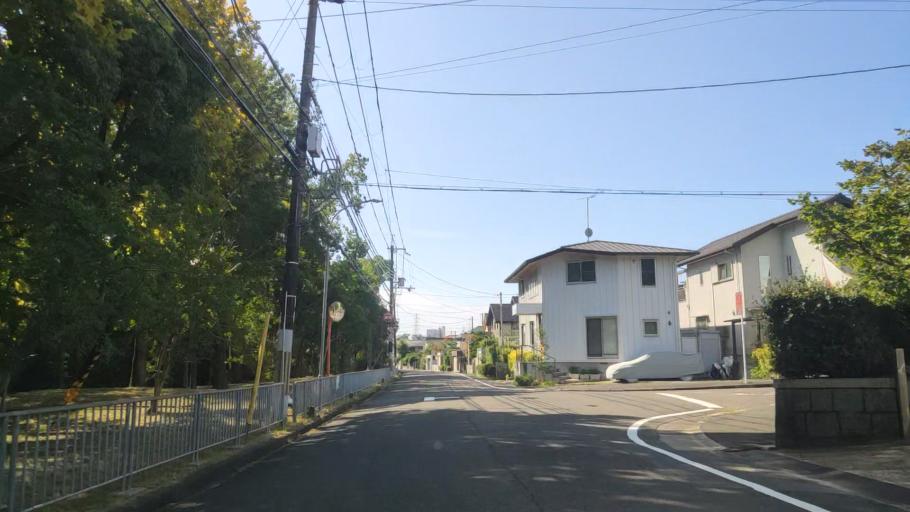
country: JP
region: Osaka
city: Mino
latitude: 34.8190
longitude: 135.5191
